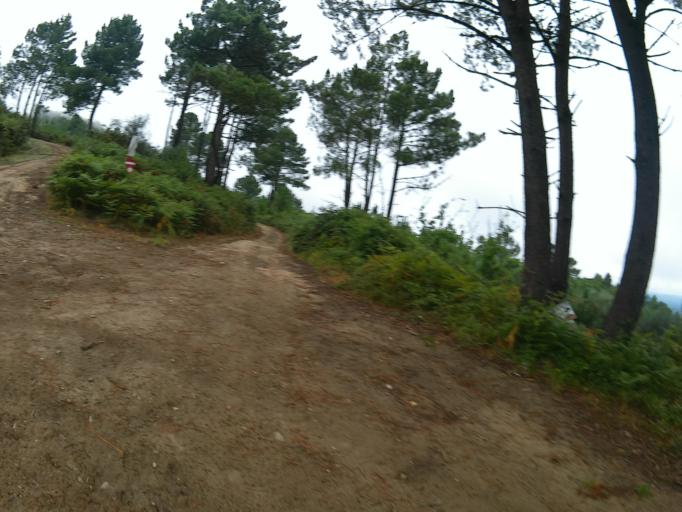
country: PT
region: Viana do Castelo
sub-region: Ponte de Lima
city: Ponte de Lima
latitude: 41.7314
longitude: -8.6053
